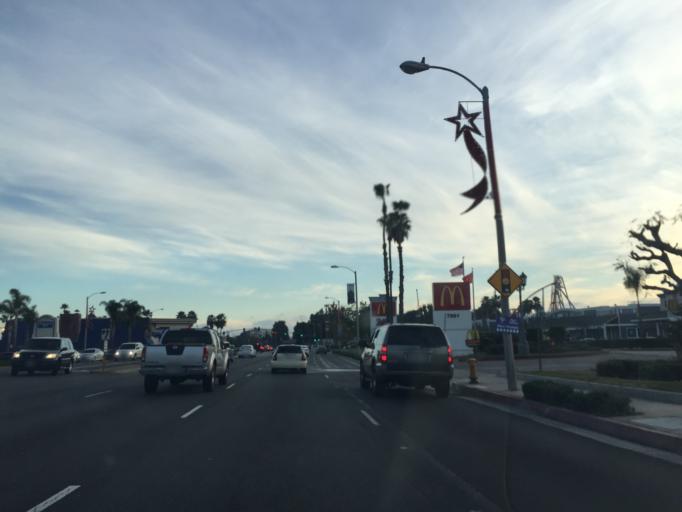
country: US
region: California
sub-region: Orange County
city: Buena Park
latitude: 33.8486
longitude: -117.9981
